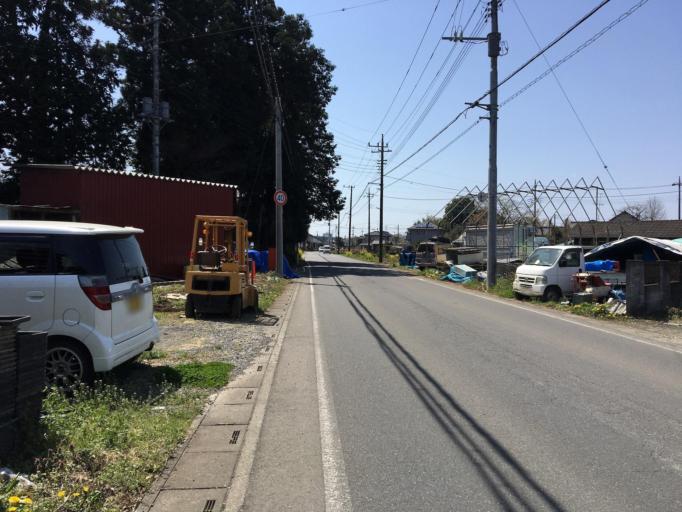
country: JP
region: Saitama
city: Sakado
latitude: 35.9446
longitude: 139.3496
